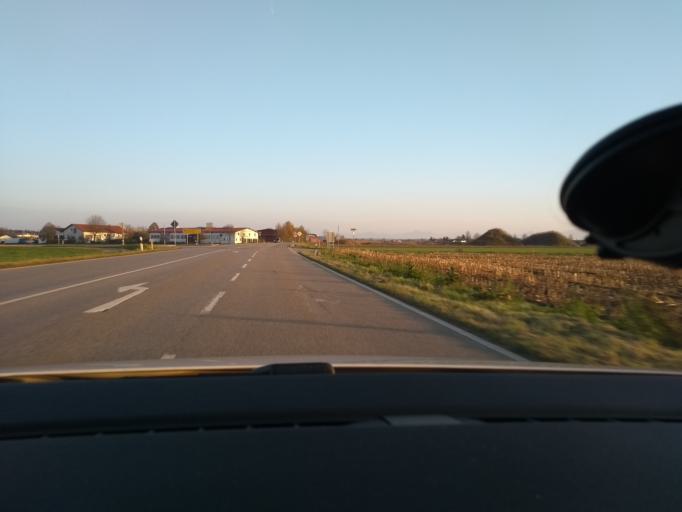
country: DE
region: Bavaria
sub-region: Upper Bavaria
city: Eiselfing
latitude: 48.0398
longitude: 12.2333
